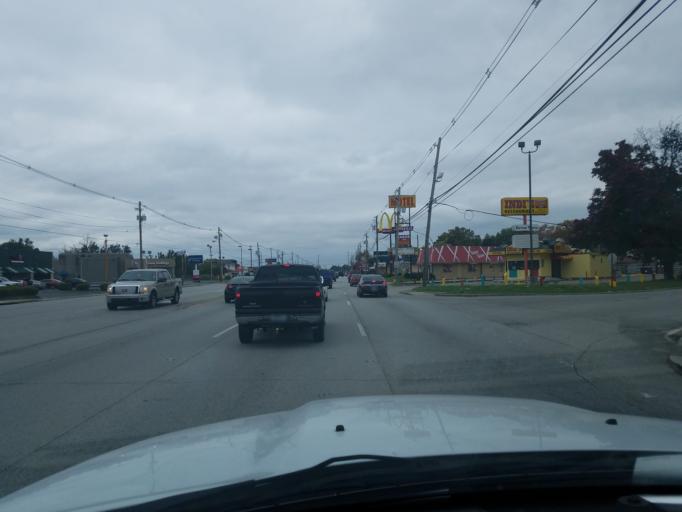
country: US
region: Kentucky
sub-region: Jefferson County
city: Shively
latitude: 38.1781
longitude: -85.8192
